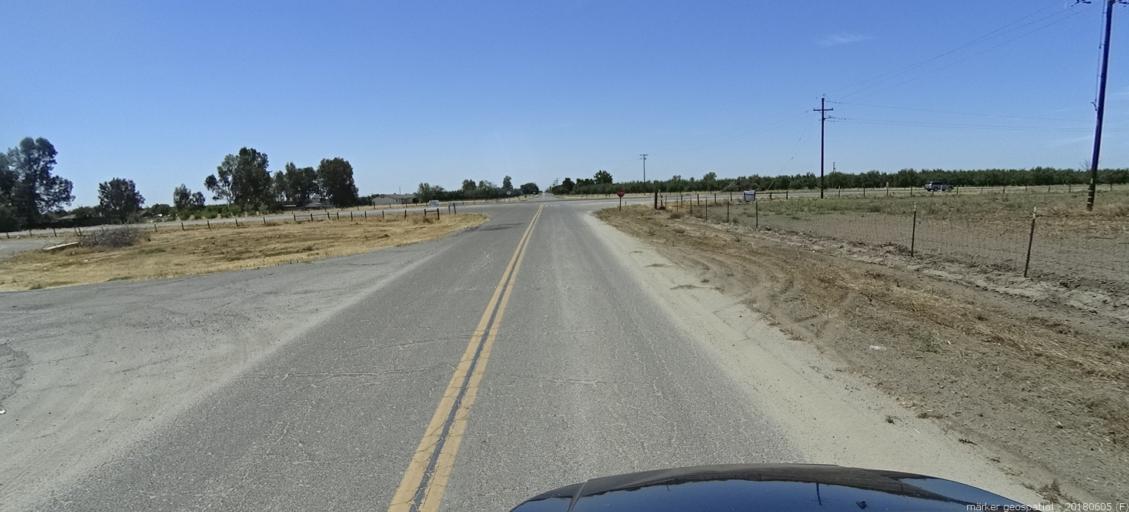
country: US
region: California
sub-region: Madera County
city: Chowchilla
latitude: 37.0844
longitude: -120.4371
